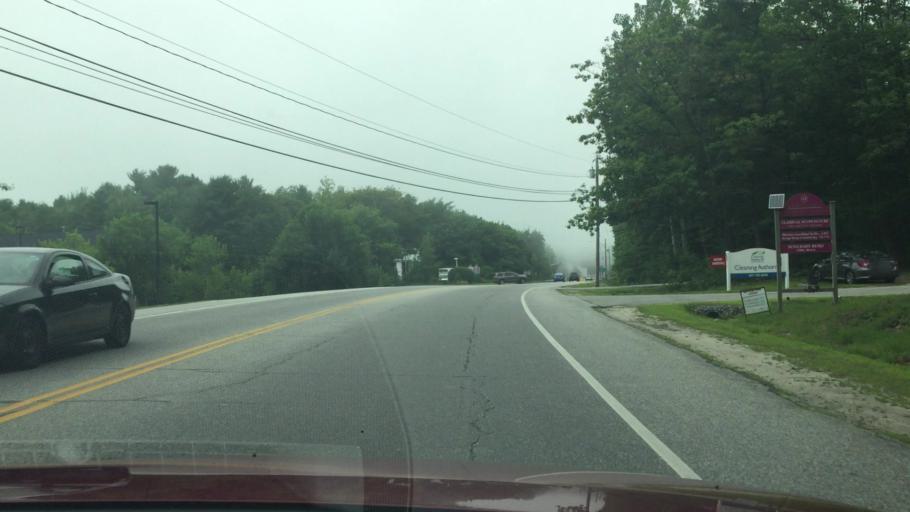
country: US
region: Maine
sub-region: Cumberland County
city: Freeport
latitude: 43.8617
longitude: -70.1045
